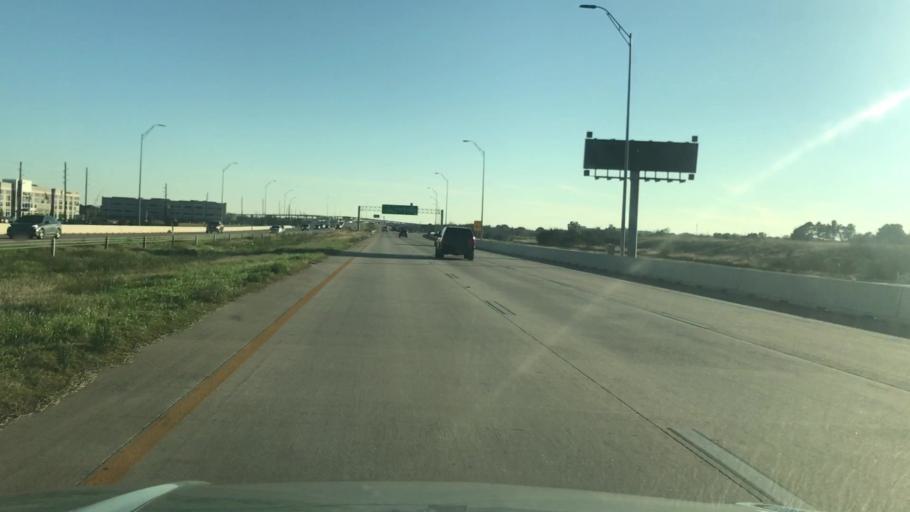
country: US
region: Texas
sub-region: Harris County
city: Katy
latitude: 29.8101
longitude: -95.7740
